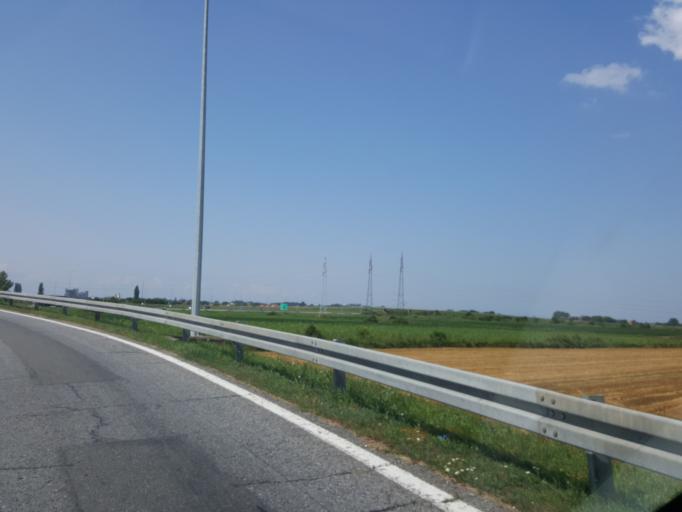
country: RS
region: Autonomna Pokrajina Vojvodina
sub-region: Sremski Okrug
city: Sremska Mitrovica
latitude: 45.0007
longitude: 19.6513
